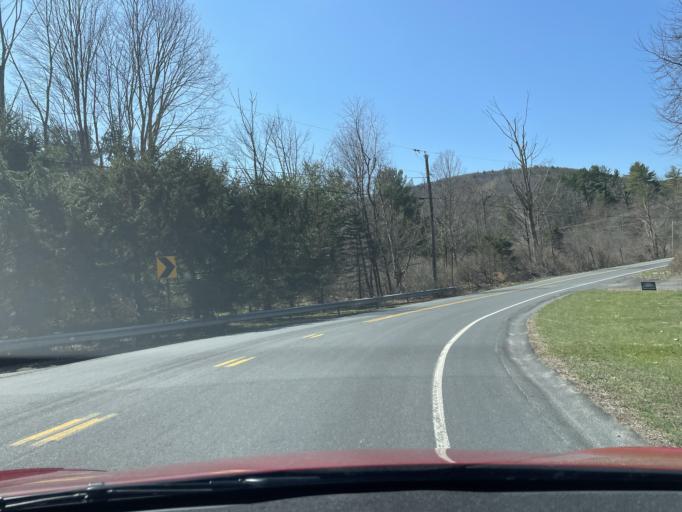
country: US
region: New York
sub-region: Ulster County
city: Woodstock
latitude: 42.0383
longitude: -74.1569
